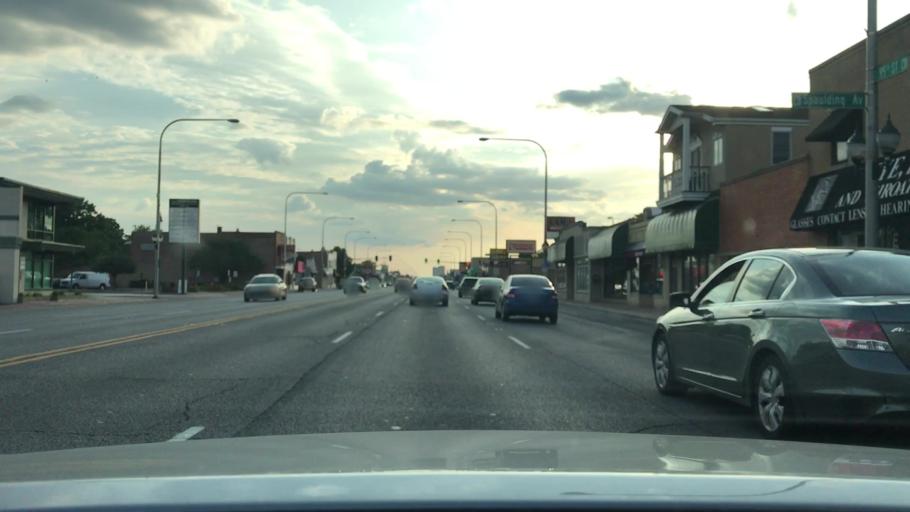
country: US
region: Illinois
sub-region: Cook County
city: Evergreen Park
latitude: 41.7208
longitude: -87.7042
